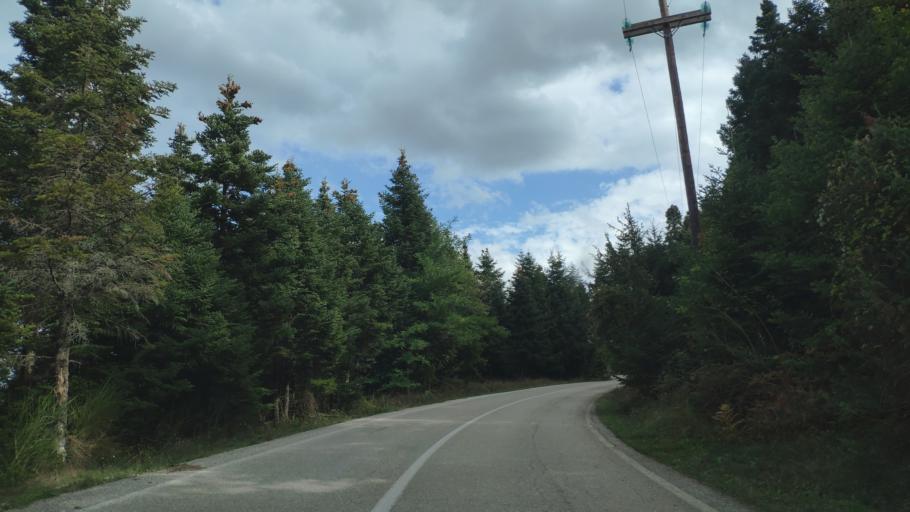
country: GR
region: Central Greece
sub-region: Nomos Fthiotidos
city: Stavros
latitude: 38.7306
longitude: 22.3465
